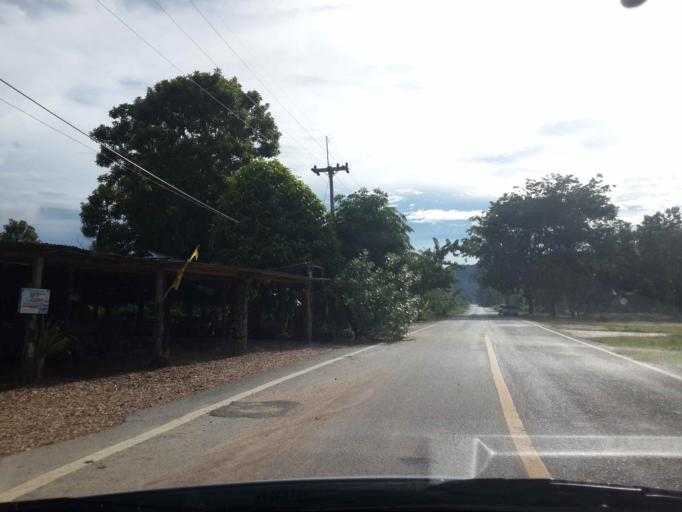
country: TH
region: Kanchanaburi
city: Dan Makham Tia
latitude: 13.8173
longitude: 99.1741
